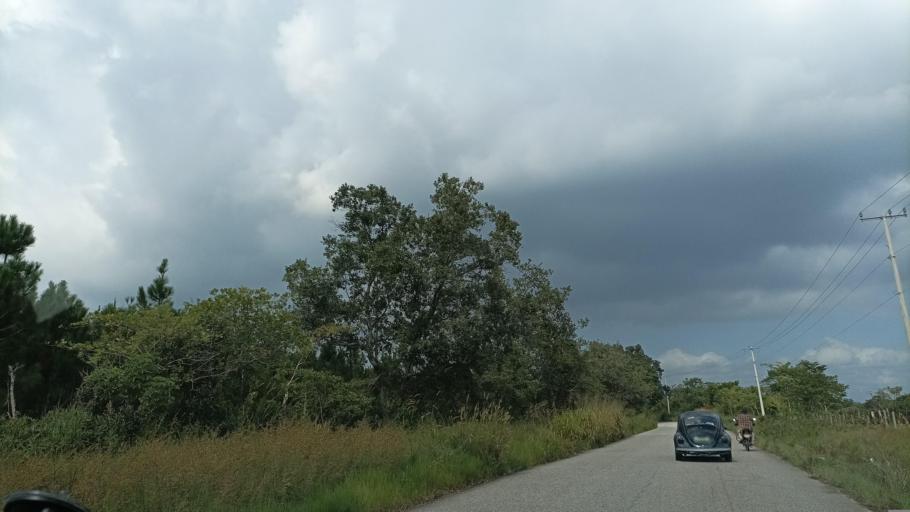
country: MX
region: Veracruz
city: Las Choapas
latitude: 17.8187
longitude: -94.1095
